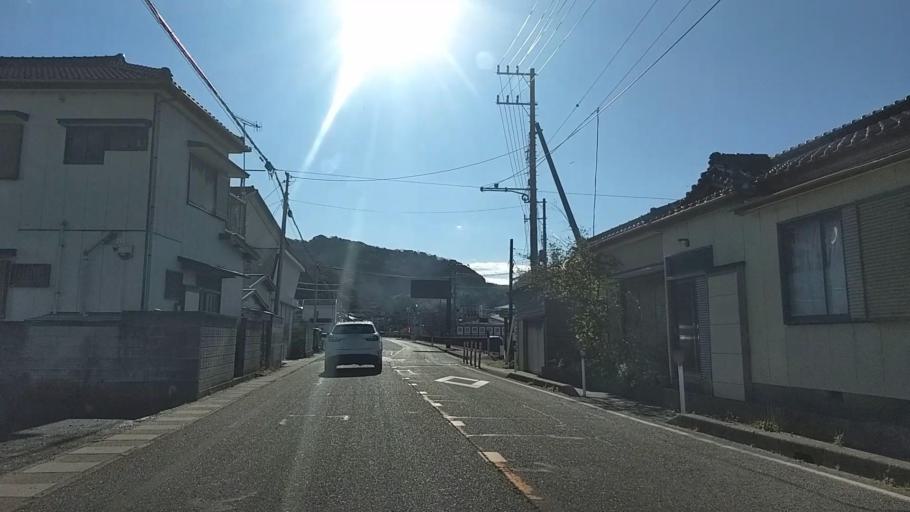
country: JP
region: Chiba
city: Tateyama
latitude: 35.1333
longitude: 139.8386
